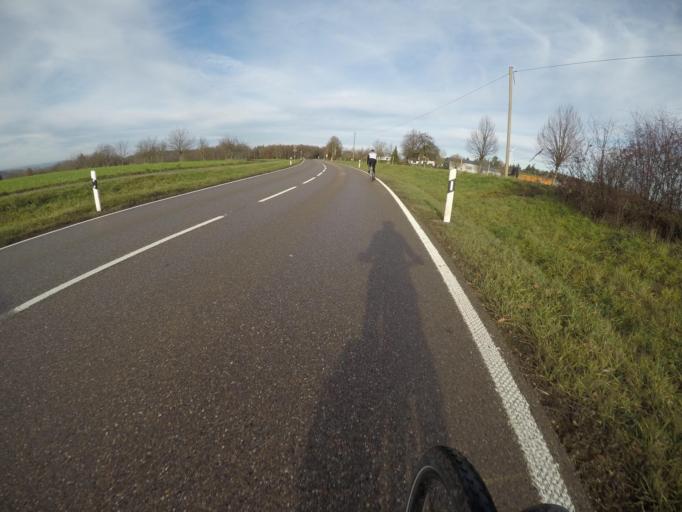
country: DE
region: Baden-Wuerttemberg
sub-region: Regierungsbezirk Stuttgart
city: Baltmannsweiler
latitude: 48.7648
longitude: 9.4553
